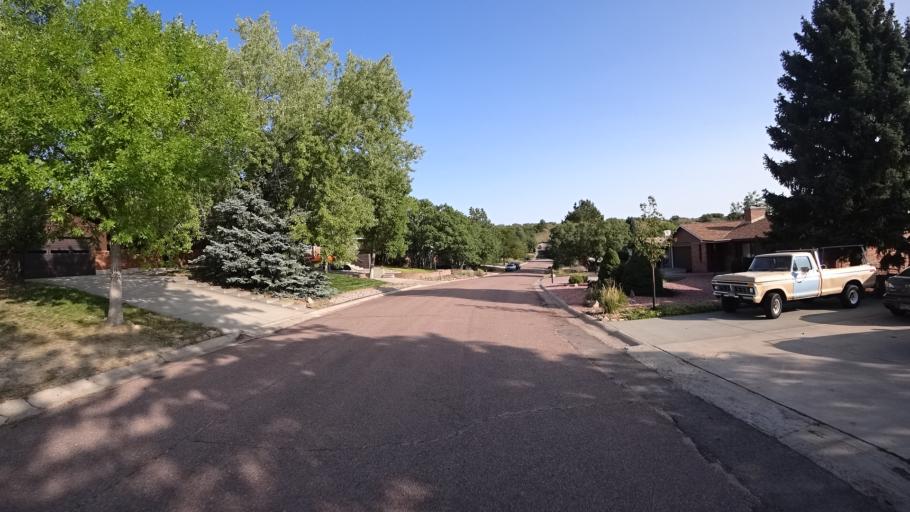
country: US
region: Colorado
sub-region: El Paso County
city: Colorado Springs
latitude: 38.8202
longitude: -104.8666
